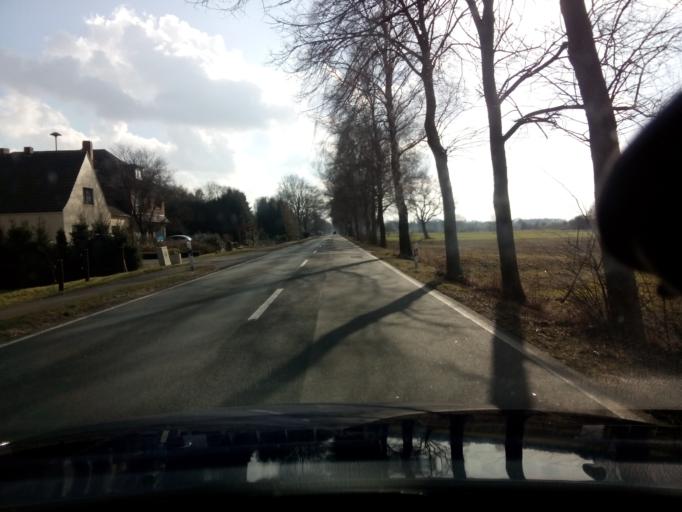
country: DE
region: Lower Saxony
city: Gnarrenburg
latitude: 53.3292
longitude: 8.9816
